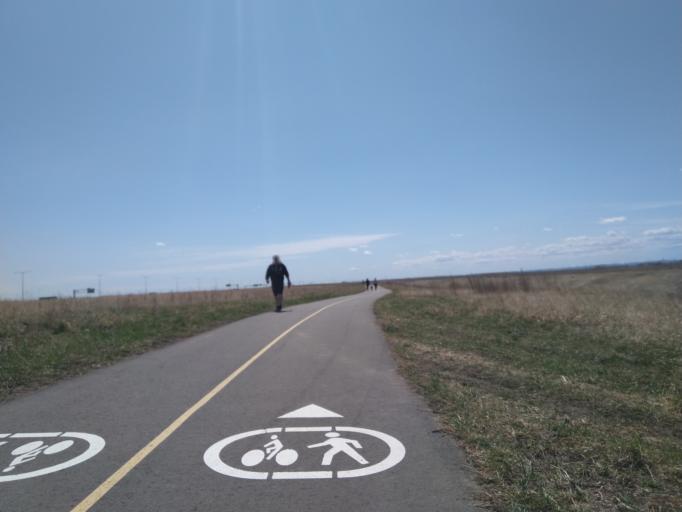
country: CA
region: Alberta
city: Chestermere
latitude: 51.0316
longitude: -113.9237
